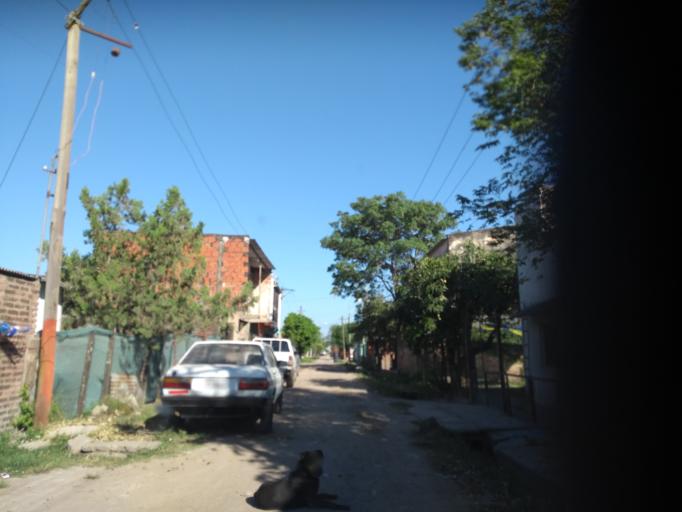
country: AR
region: Chaco
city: Resistencia
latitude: -27.4705
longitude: -58.9744
